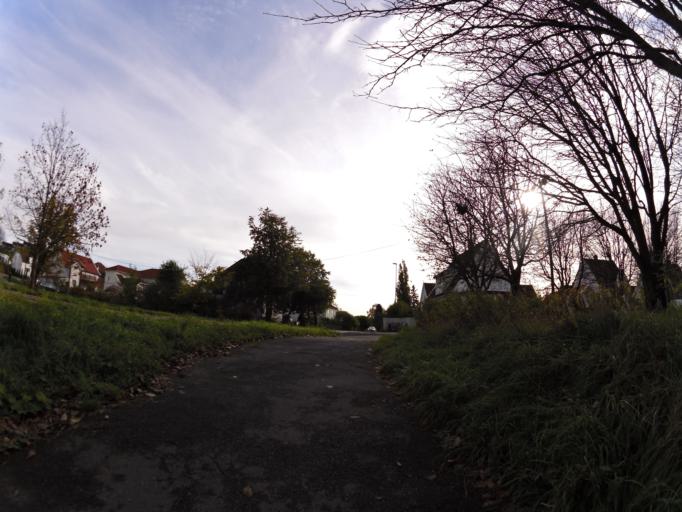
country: NO
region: Ostfold
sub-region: Fredrikstad
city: Fredrikstad
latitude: 59.2195
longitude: 10.9304
